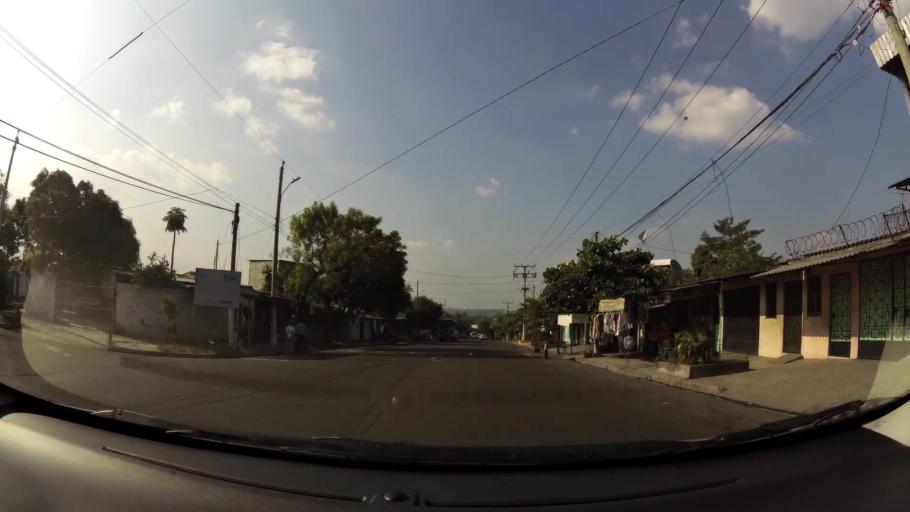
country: SV
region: San Salvador
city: Ilopango
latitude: 13.7126
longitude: -89.1059
